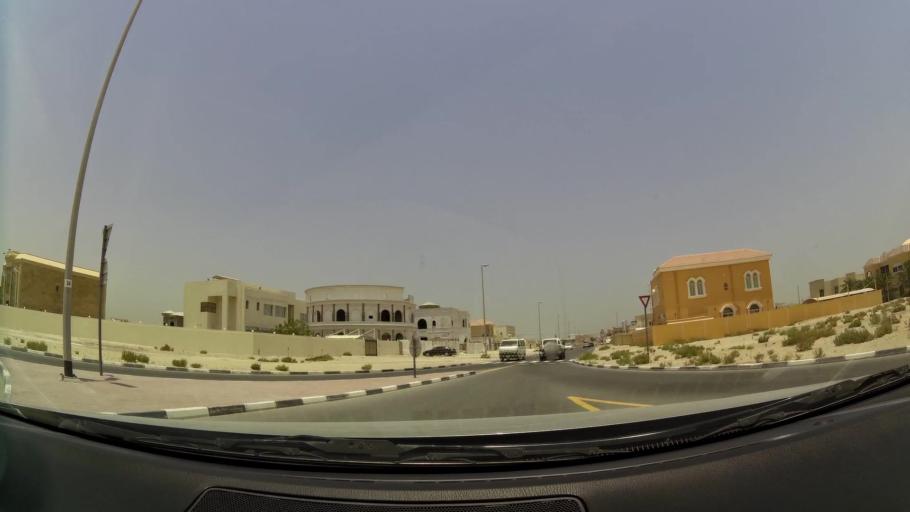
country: AE
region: Dubai
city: Dubai
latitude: 25.0894
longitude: 55.2346
